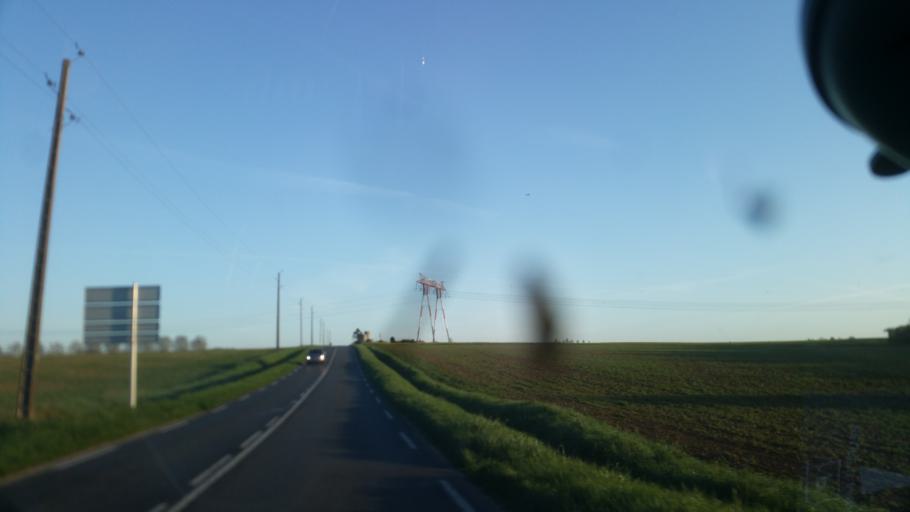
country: FR
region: Ile-de-France
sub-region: Departement de l'Essonne
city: Limours
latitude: 48.6312
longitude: 2.0659
